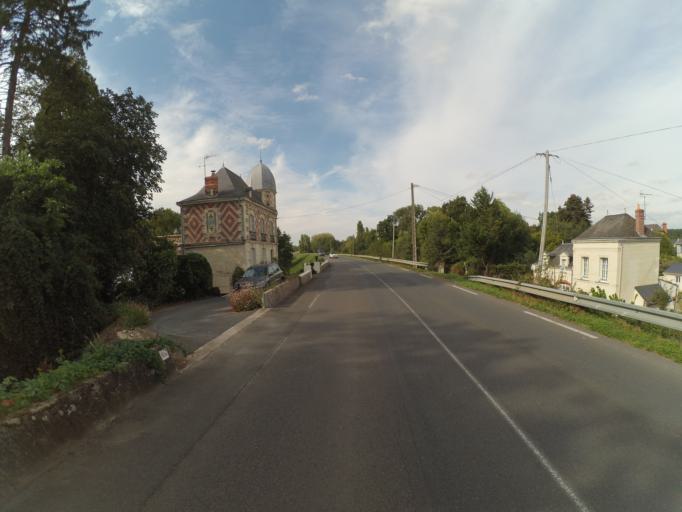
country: FR
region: Pays de la Loire
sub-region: Departement de Maine-et-Loire
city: Villebernier
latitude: 47.2512
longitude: -0.0212
